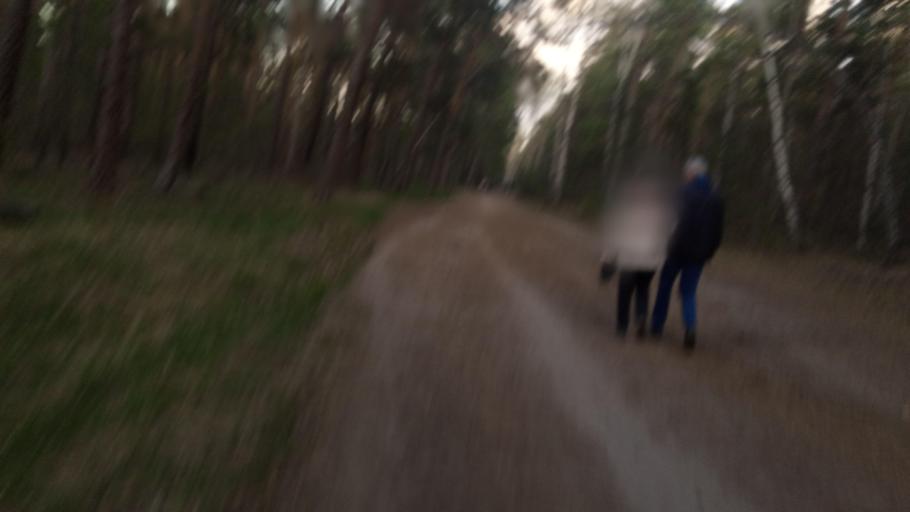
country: RU
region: Chelyabinsk
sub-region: Gorod Chelyabinsk
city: Chelyabinsk
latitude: 55.1663
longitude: 61.3508
